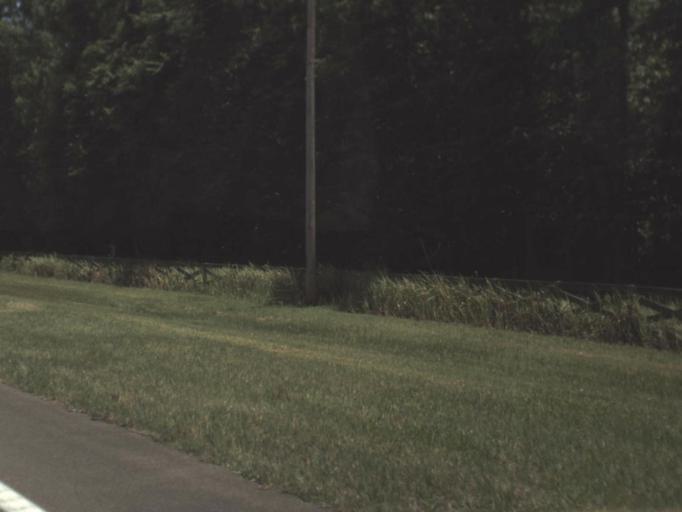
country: US
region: Florida
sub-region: Union County
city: Lake Butler
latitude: 29.9063
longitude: -82.4228
